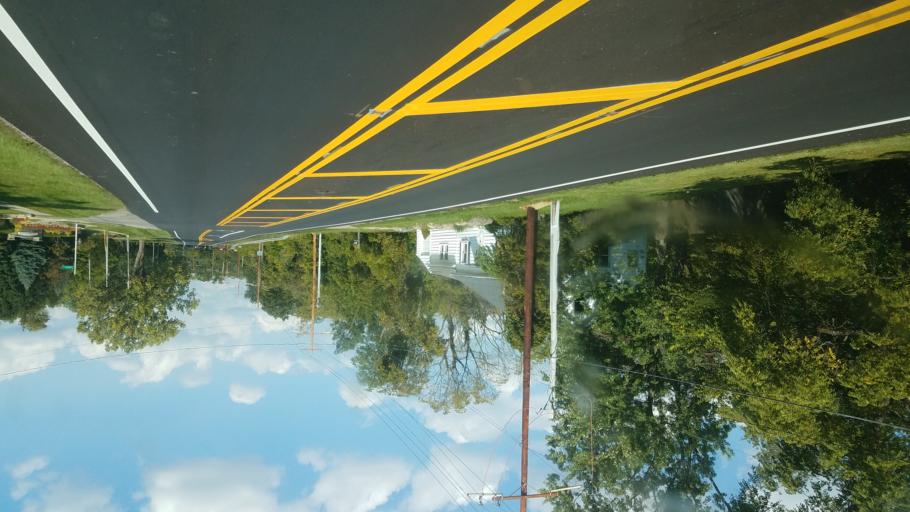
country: US
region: Ohio
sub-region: Franklin County
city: Grove City
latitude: 39.9150
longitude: -83.1041
